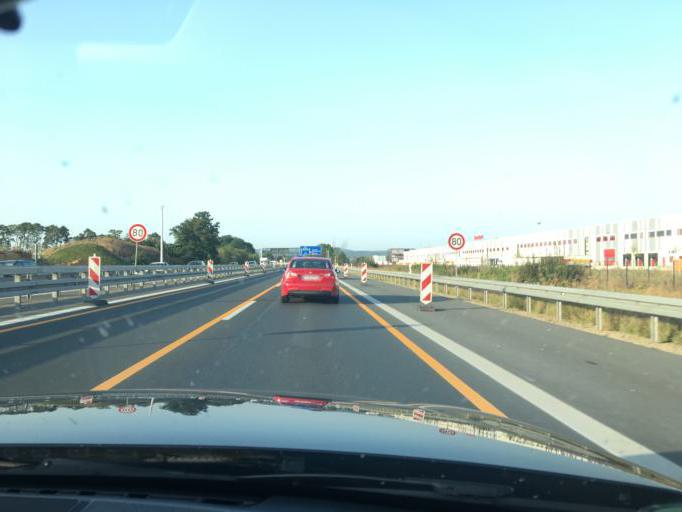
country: DE
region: Bavaria
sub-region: Upper Franconia
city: Hausen
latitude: 49.6876
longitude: 11.0580
